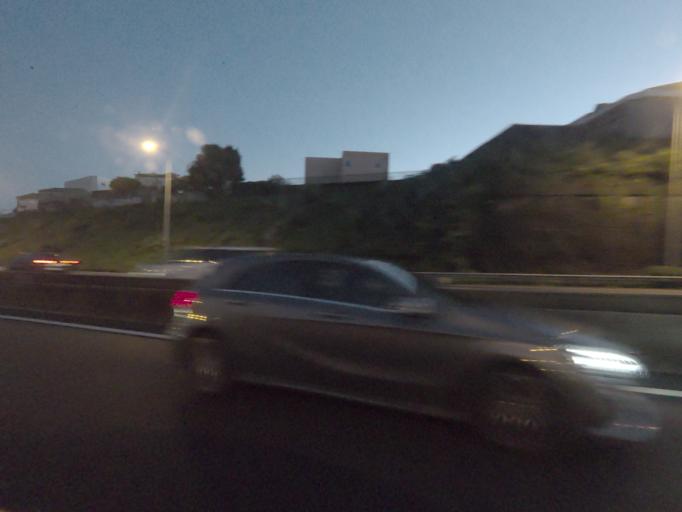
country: PT
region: Porto
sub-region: Porto
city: Porto
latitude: 41.1741
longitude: -8.6097
